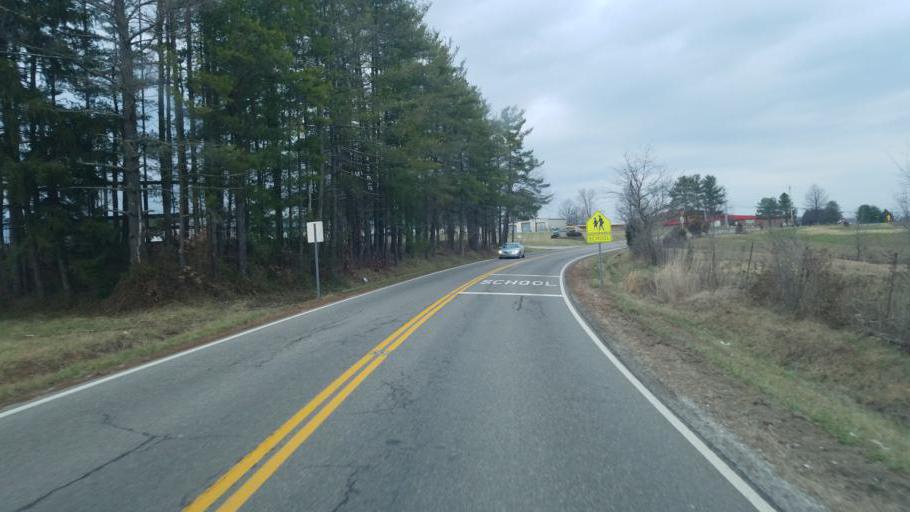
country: US
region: Ohio
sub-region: Jackson County
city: Oak Hill
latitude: 38.8202
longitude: -82.4016
